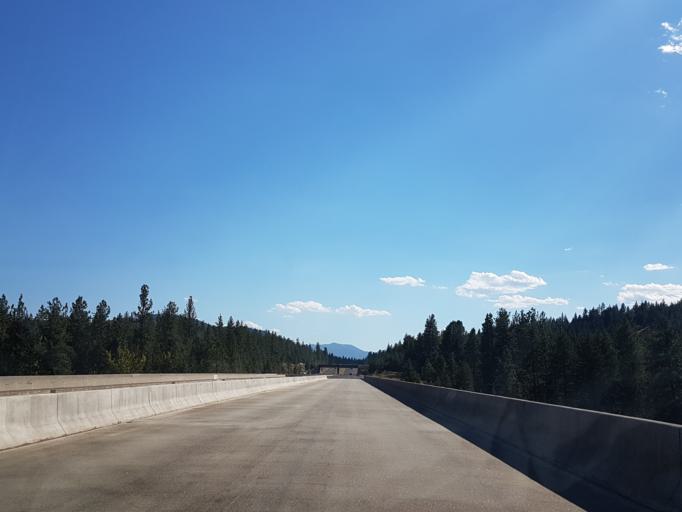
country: US
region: Montana
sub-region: Mineral County
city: Superior
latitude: 47.1315
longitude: -114.7971
